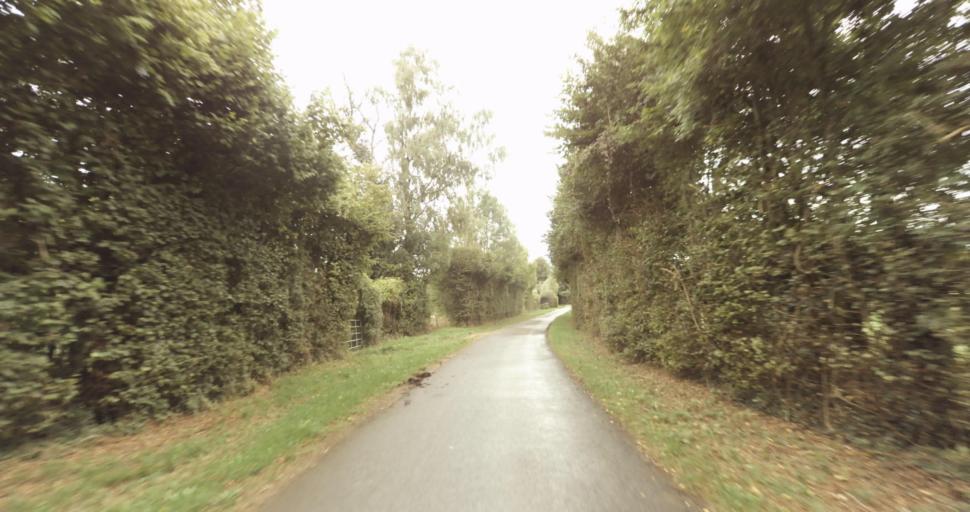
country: FR
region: Lower Normandy
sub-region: Departement de l'Orne
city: Sainte-Gauburge-Sainte-Colombe
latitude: 48.7294
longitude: 0.3704
